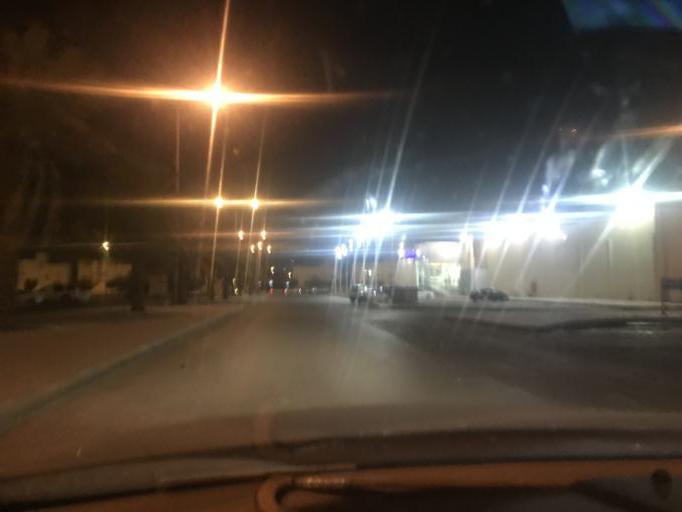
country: SA
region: Ar Riyad
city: Riyadh
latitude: 24.6763
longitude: 46.7802
